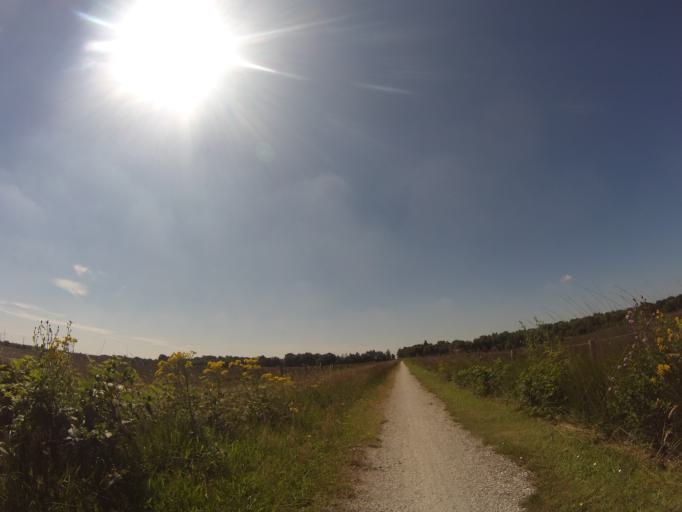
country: DE
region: Lower Saxony
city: Twist
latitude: 52.6735
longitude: 7.0231
